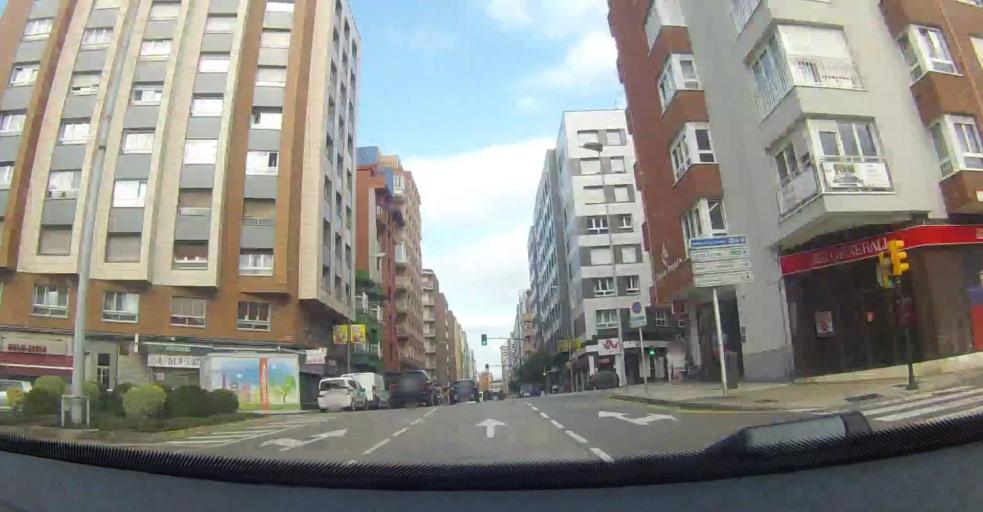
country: ES
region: Asturias
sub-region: Province of Asturias
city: Gijon
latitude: 43.5363
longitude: -5.6597
